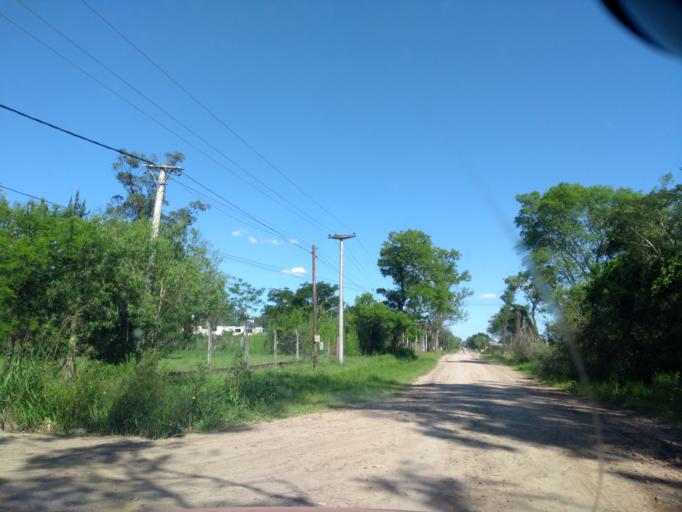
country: AR
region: Chaco
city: Resistencia
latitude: -27.4229
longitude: -58.9465
